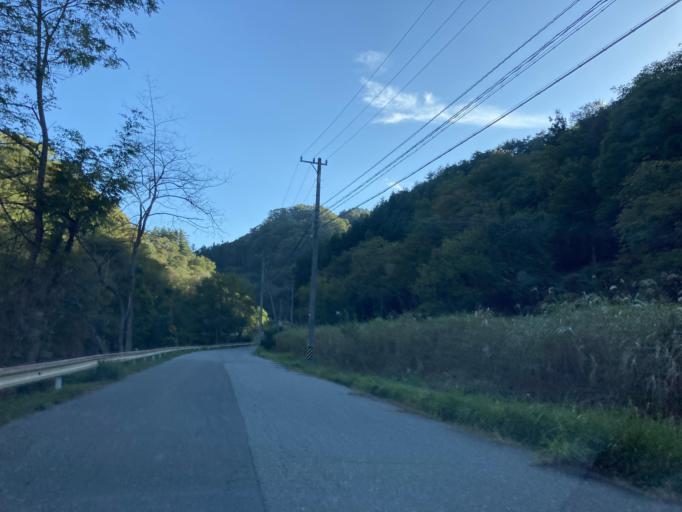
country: JP
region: Nagano
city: Omachi
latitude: 36.4575
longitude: 137.9640
